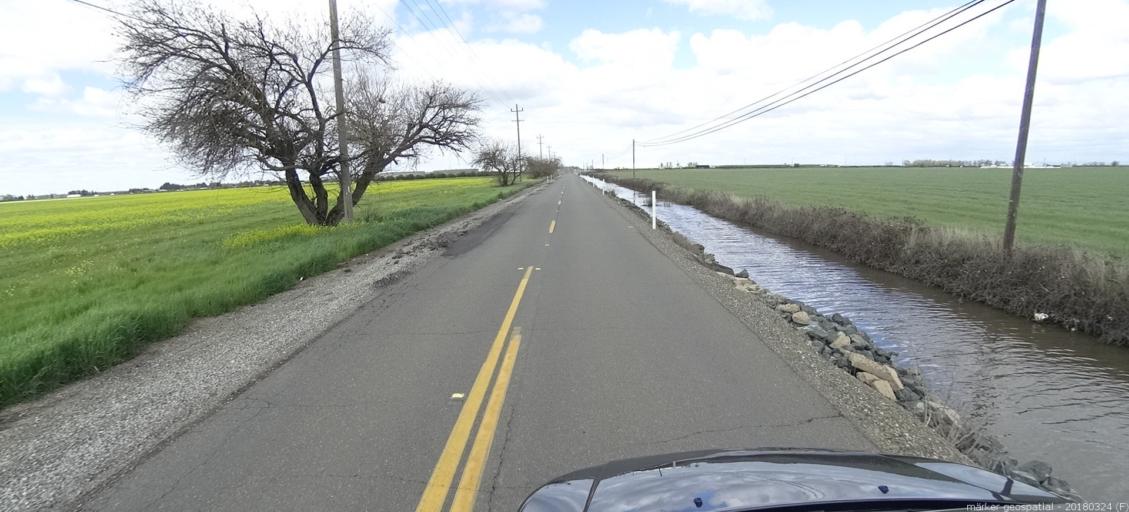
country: US
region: California
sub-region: Yolo County
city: West Sacramento
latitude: 38.6651
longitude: -121.5764
